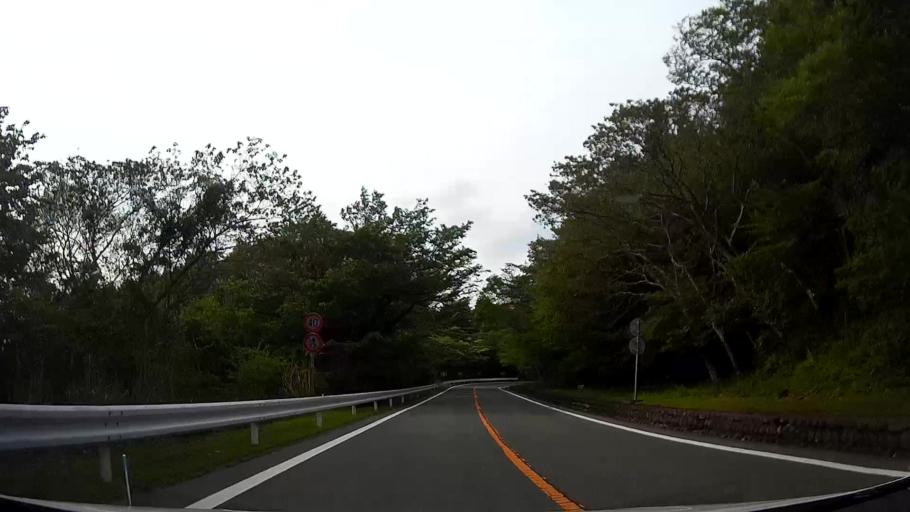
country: JP
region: Shizuoka
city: Ito
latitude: 34.9980
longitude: 139.0362
